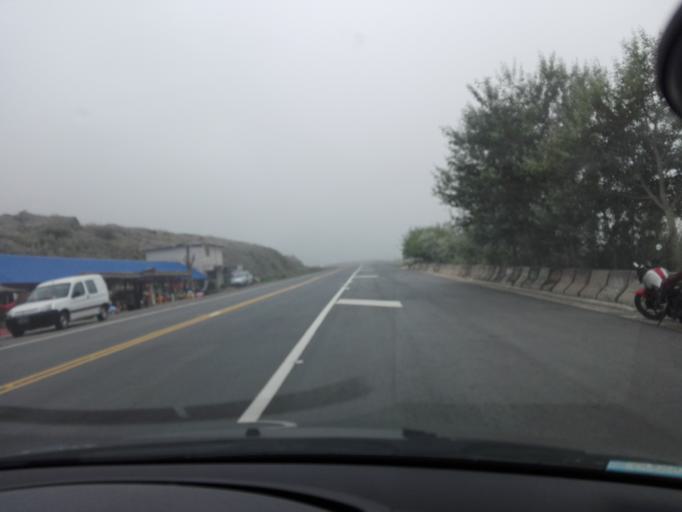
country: AR
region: Cordoba
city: Cuesta Blanca
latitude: -31.5983
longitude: -64.7136
